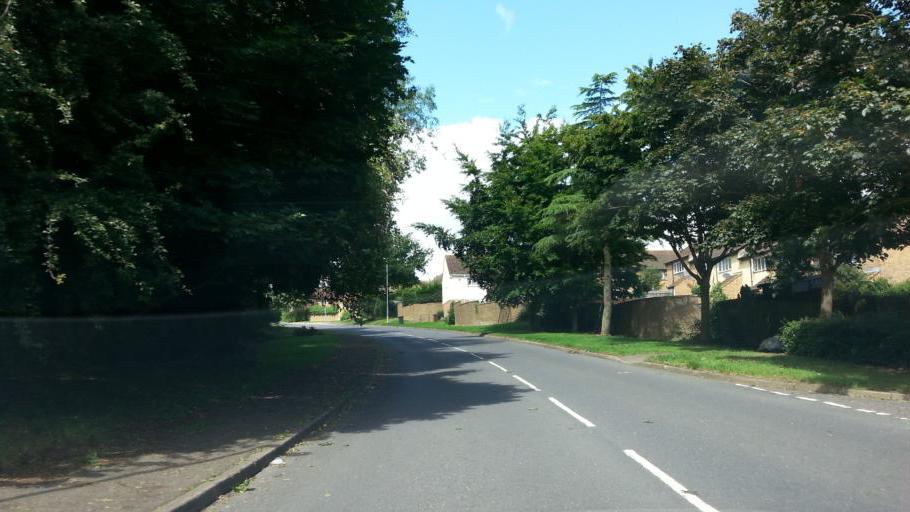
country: GB
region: England
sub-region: Northamptonshire
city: Earls Barton
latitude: 52.2696
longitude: -0.8080
